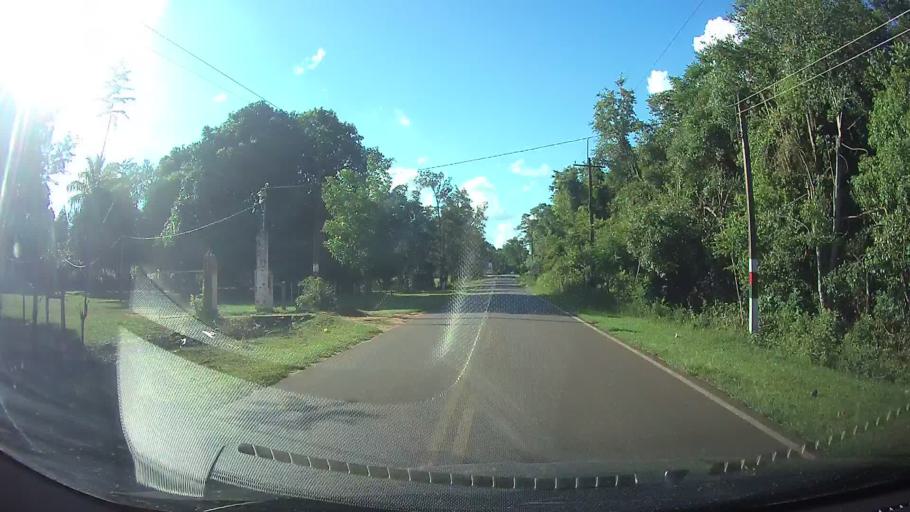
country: PY
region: Central
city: Aregua
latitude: -25.3308
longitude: -57.3840
